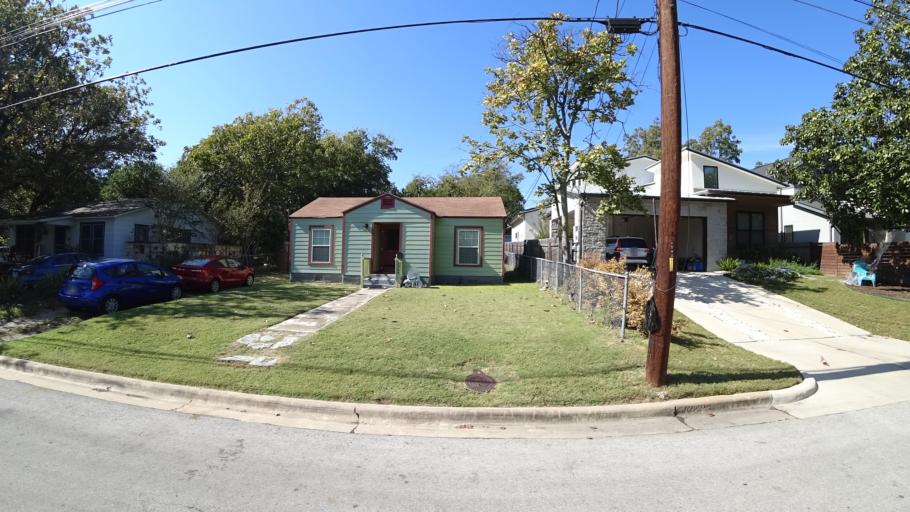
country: US
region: Texas
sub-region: Travis County
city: Austin
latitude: 30.2543
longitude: -97.7681
